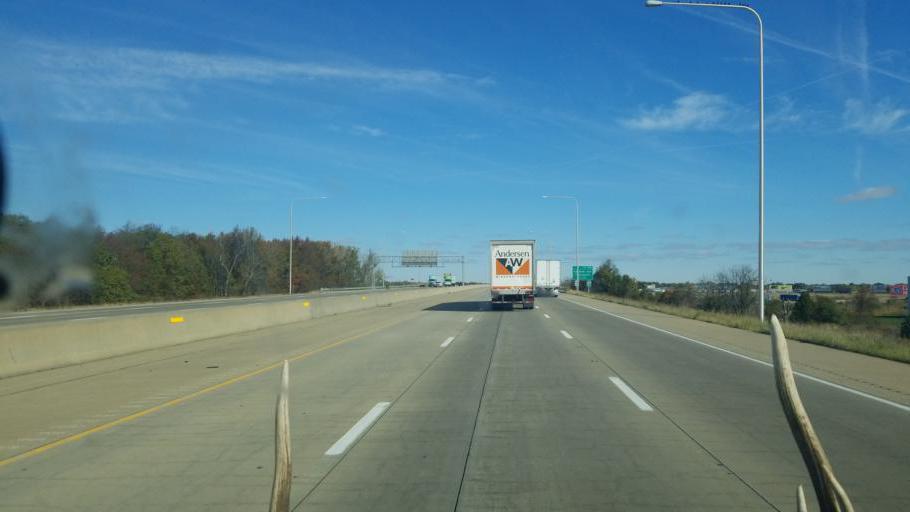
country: US
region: Illinois
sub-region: Effingham County
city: Effingham
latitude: 39.1079
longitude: -88.5725
